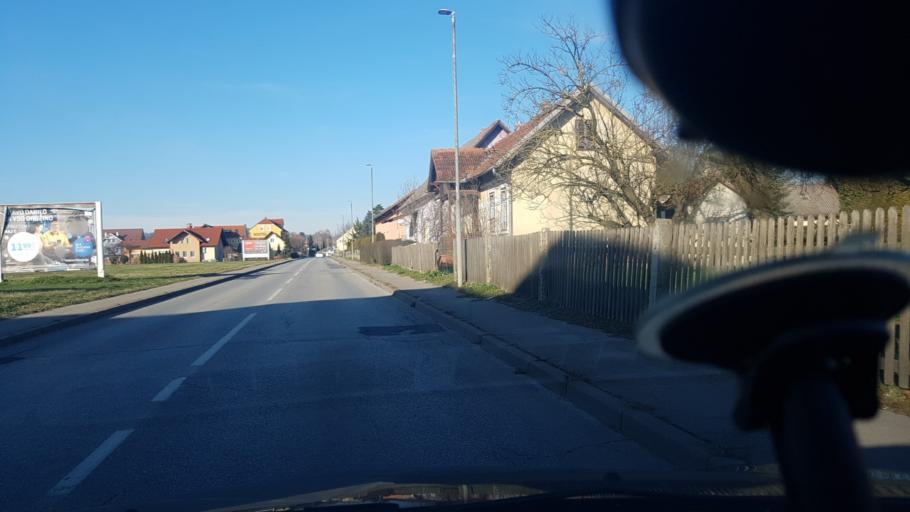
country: SI
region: Ptuj
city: Ptuj
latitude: 46.4120
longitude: 15.8650
